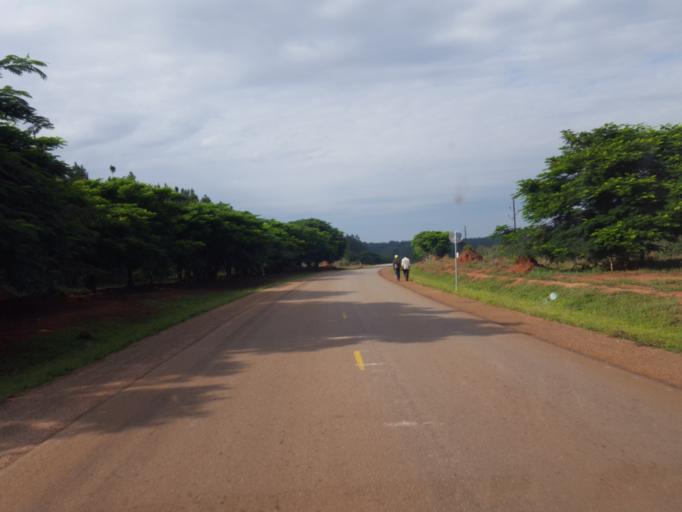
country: UG
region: Central Region
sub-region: Kyankwanzi District
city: Kyankwanzi
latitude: 1.2047
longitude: 31.5615
